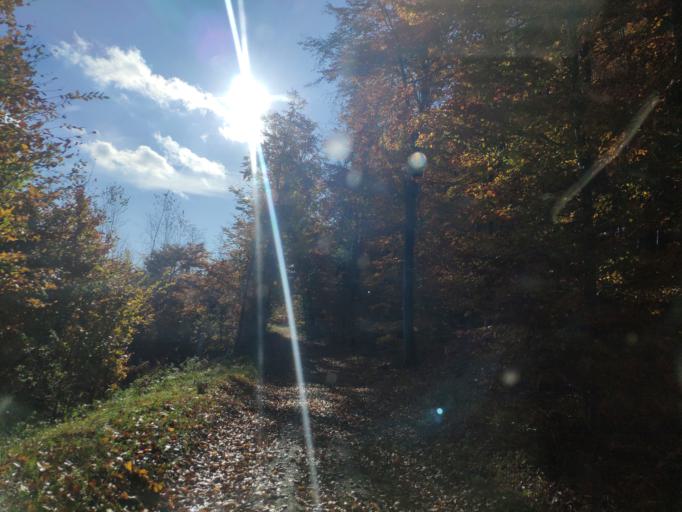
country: SK
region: Kosicky
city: Moldava nad Bodvou
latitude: 48.7320
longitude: 21.0267
